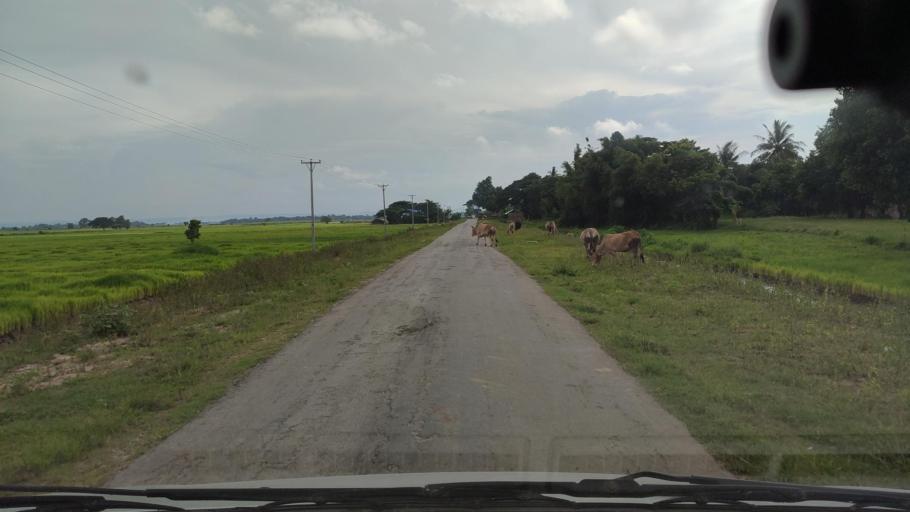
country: MM
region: Bago
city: Pyu
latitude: 18.5576
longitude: 96.6021
